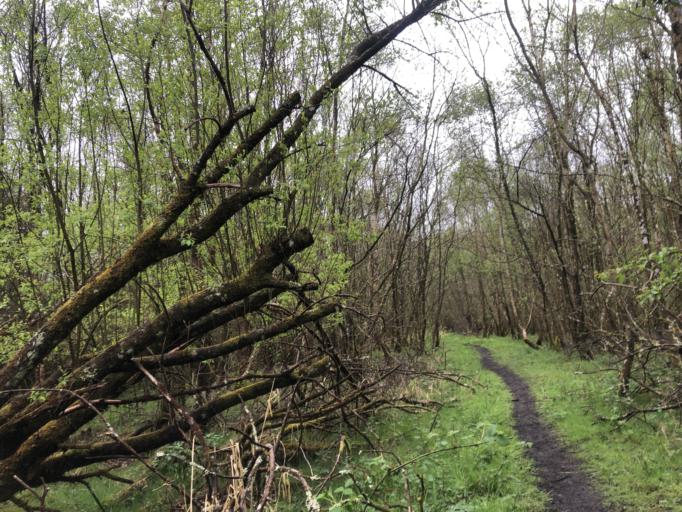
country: IE
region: Connaught
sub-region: County Leitrim
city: Carrick-on-Shannon
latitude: 53.9892
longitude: -8.1814
